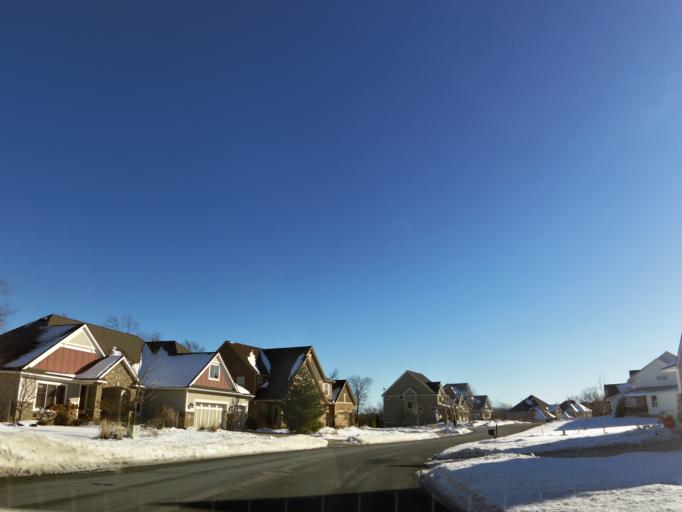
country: US
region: Minnesota
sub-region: Scott County
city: Prior Lake
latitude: 44.7415
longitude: -93.4536
